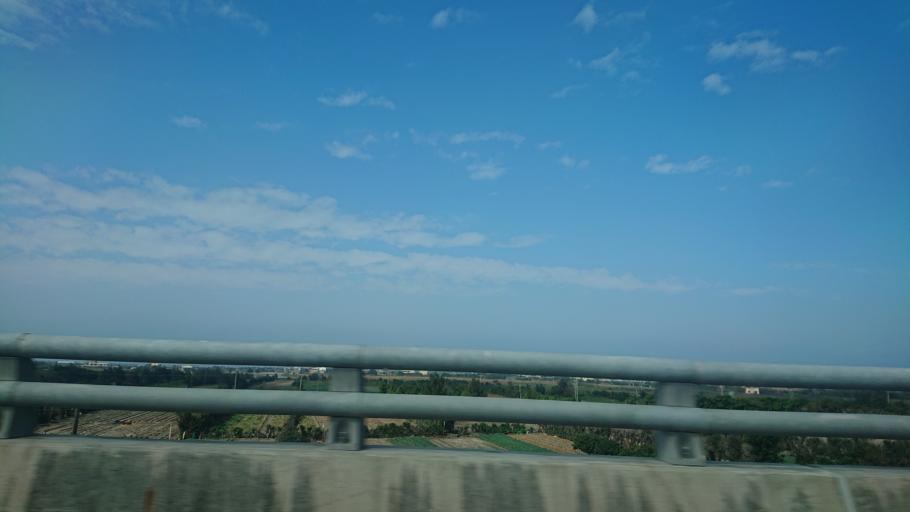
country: TW
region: Taiwan
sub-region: Changhua
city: Chang-hua
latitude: 23.9816
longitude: 120.3650
